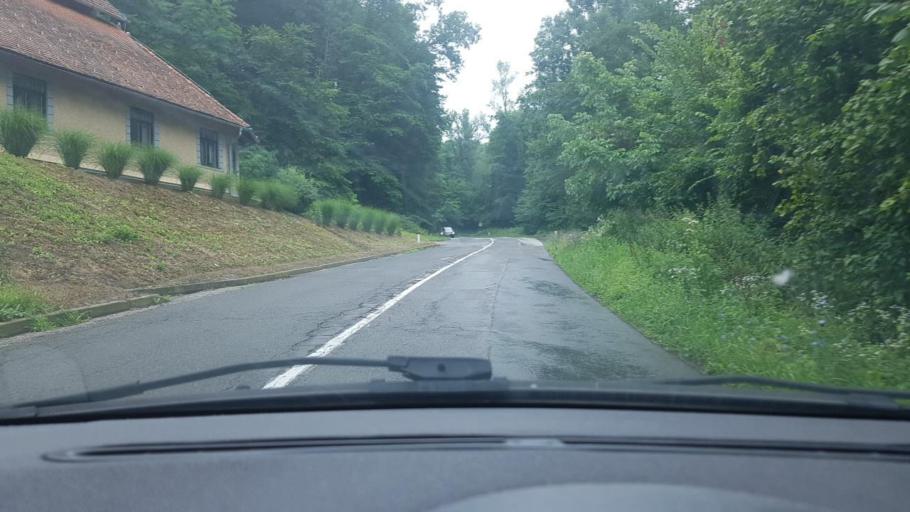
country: AT
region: Styria
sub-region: Politischer Bezirk Suedoststeiermark
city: Mureck
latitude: 46.7043
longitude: 15.7840
